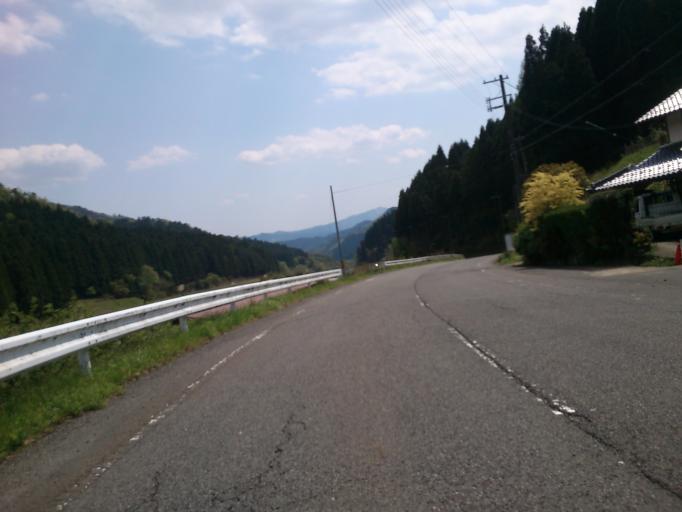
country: JP
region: Hyogo
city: Toyooka
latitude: 35.3875
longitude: 134.9403
